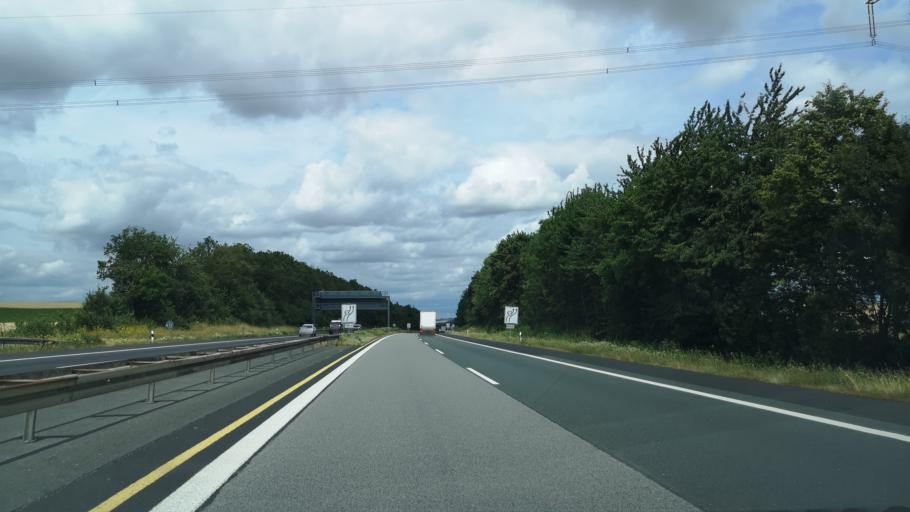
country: DE
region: Bavaria
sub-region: Regierungsbezirk Unterfranken
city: Rottendorf
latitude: 49.7934
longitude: 10.0592
